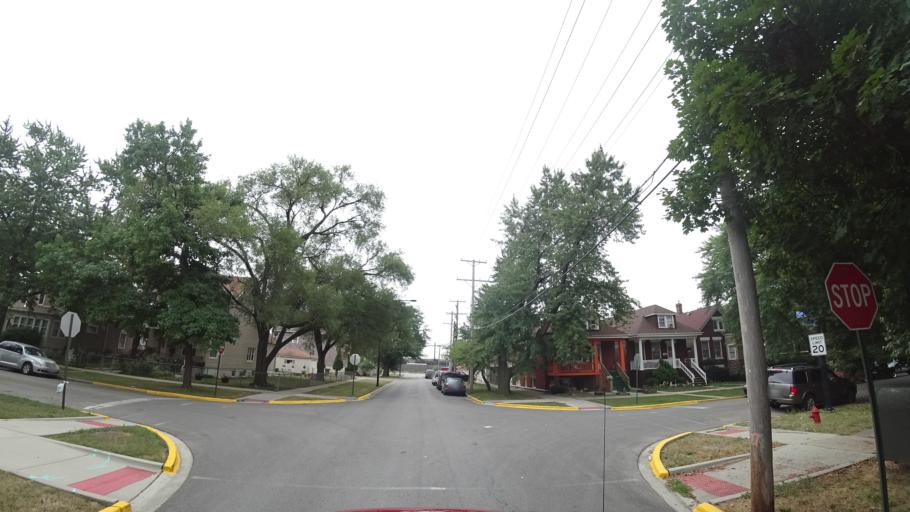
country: US
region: Illinois
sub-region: Cook County
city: Cicero
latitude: 41.8449
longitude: -87.7514
